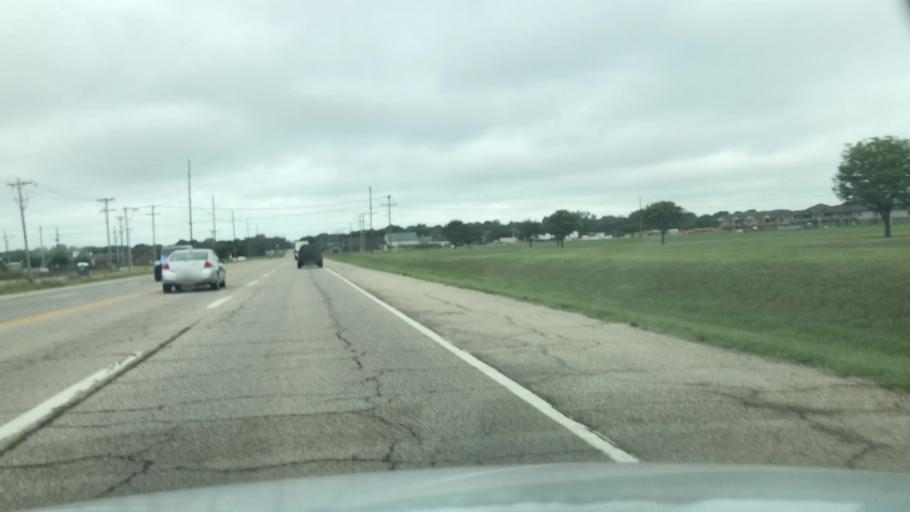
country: US
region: Oklahoma
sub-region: Washington County
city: Dewey
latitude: 36.7280
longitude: -95.8969
